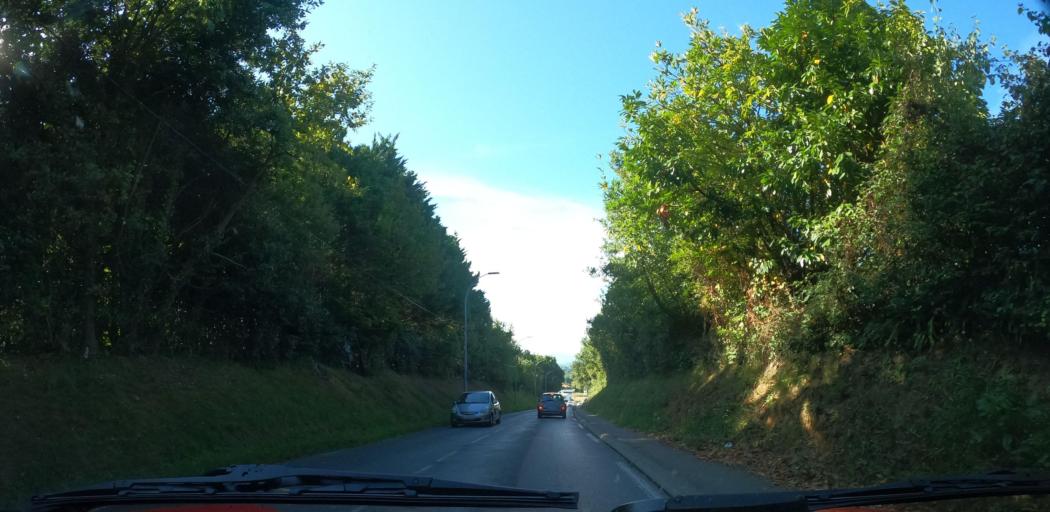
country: FR
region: Aquitaine
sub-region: Departement des Pyrenees-Atlantiques
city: Arbonne
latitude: 43.4490
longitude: -1.5443
